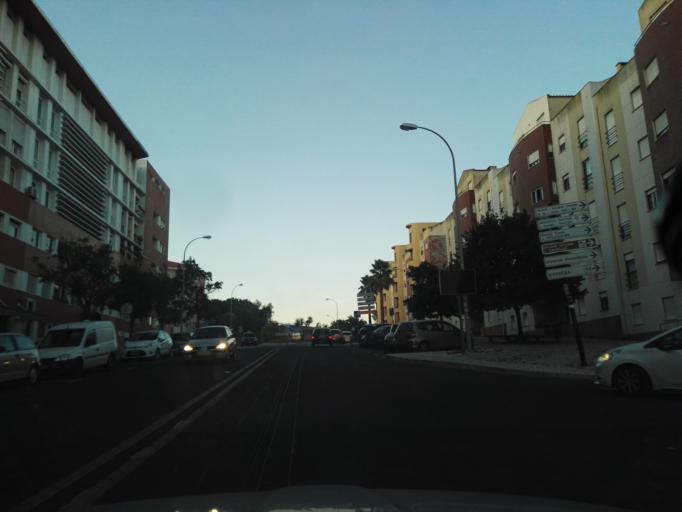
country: PT
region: Lisbon
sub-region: Amadora
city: Amadora
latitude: 38.7322
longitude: -9.2162
